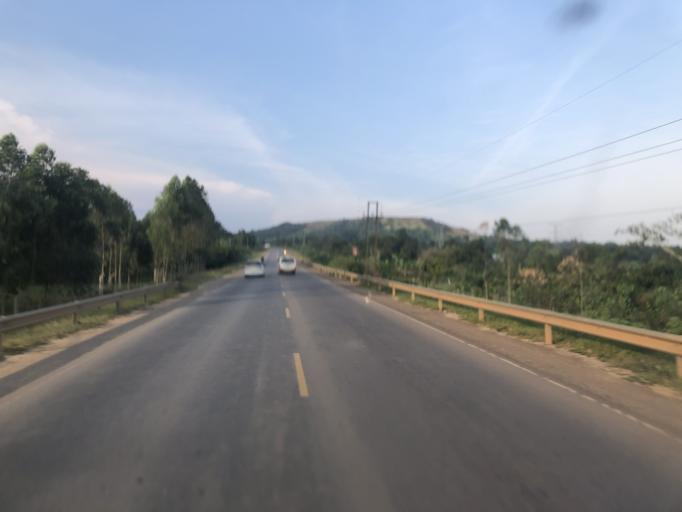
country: UG
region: Central Region
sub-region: Mpigi District
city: Mpigi
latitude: 0.1869
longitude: 32.2895
